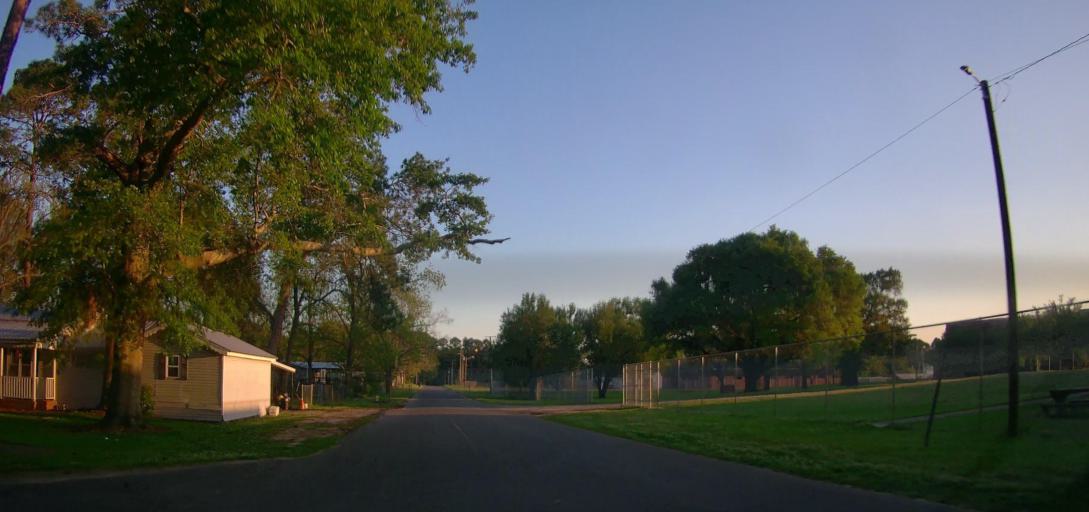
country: US
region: Georgia
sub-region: Ben Hill County
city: Fitzgerald
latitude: 31.7090
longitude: -83.2598
